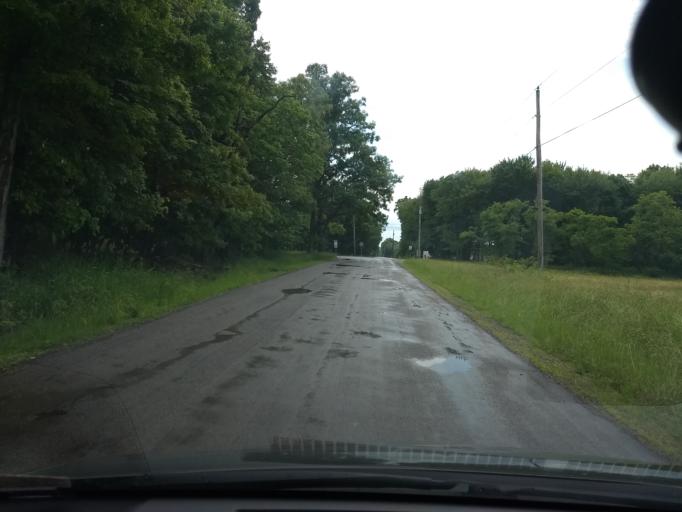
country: US
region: Pennsylvania
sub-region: Armstrong County
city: Orchard Hills
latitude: 40.5569
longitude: -79.5111
